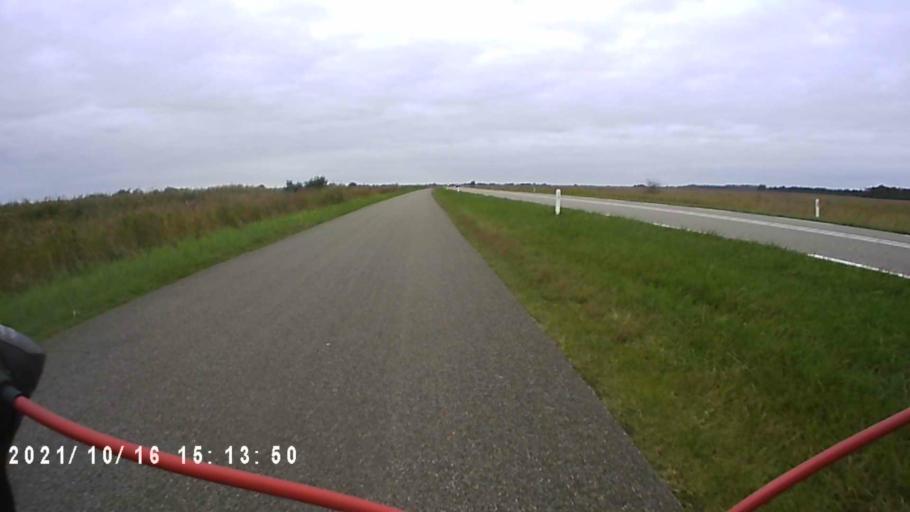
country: NL
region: Groningen
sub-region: Gemeente De Marne
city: Ulrum
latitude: 53.3646
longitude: 6.2545
